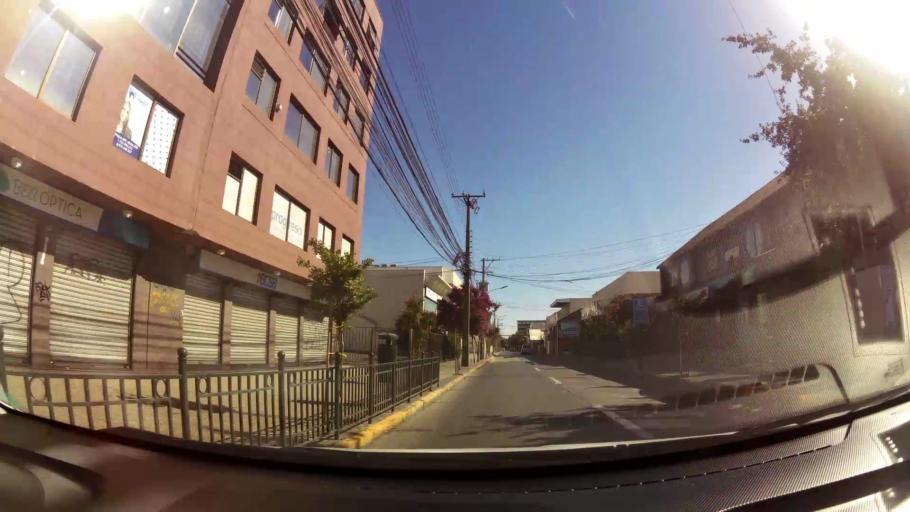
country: CL
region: O'Higgins
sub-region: Provincia de Cachapoal
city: Rancagua
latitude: -34.1675
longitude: -70.7430
